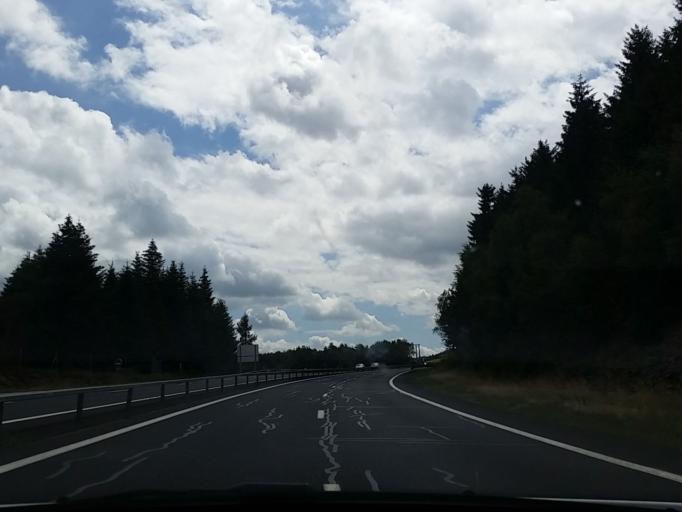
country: FR
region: Auvergne
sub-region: Departement du Cantal
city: Saint-Flour
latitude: 45.1257
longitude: 3.1388
